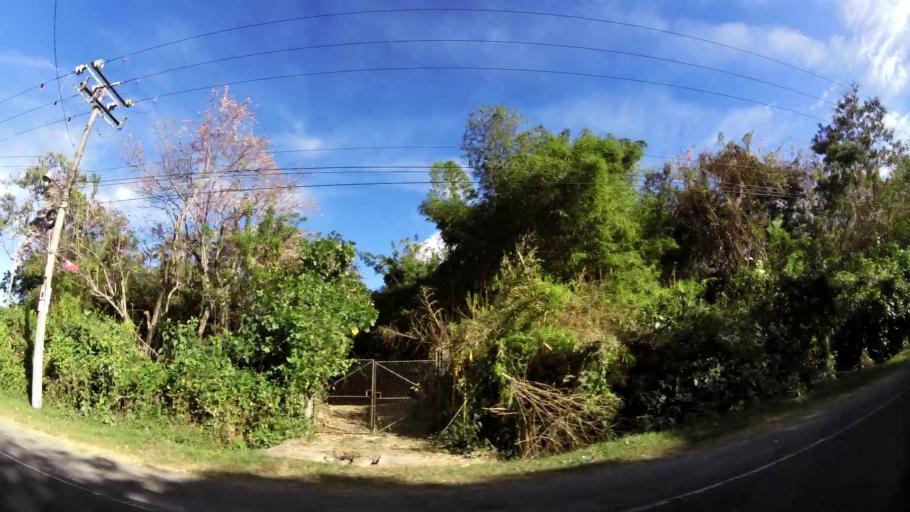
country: SV
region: Cuscatlan
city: Tecoluca
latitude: 13.7689
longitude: -89.0452
